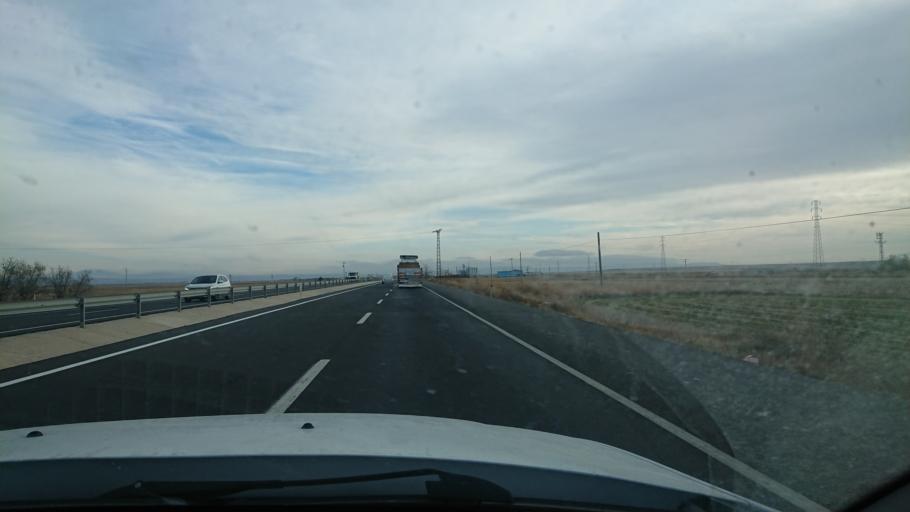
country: TR
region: Aksaray
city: Yesilova
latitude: 38.3161
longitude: 33.8509
